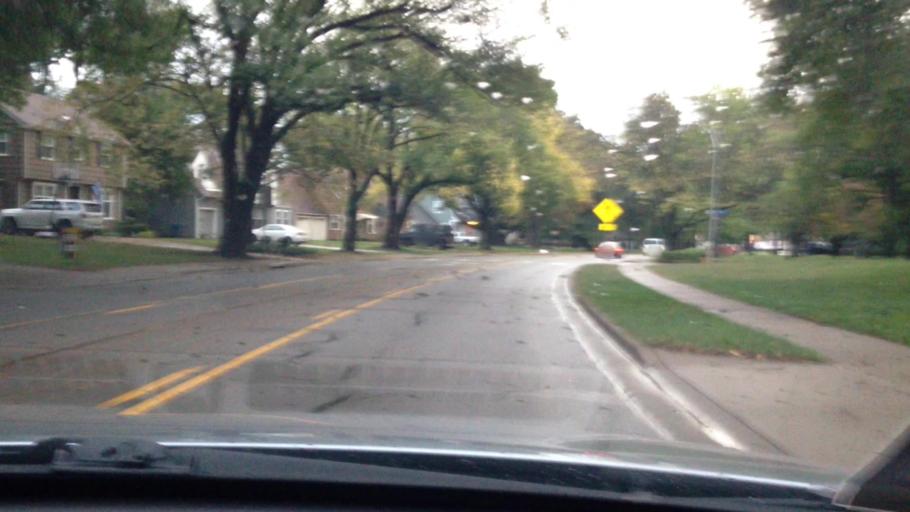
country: US
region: Kansas
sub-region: Johnson County
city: Leawood
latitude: 38.9871
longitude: -94.6092
